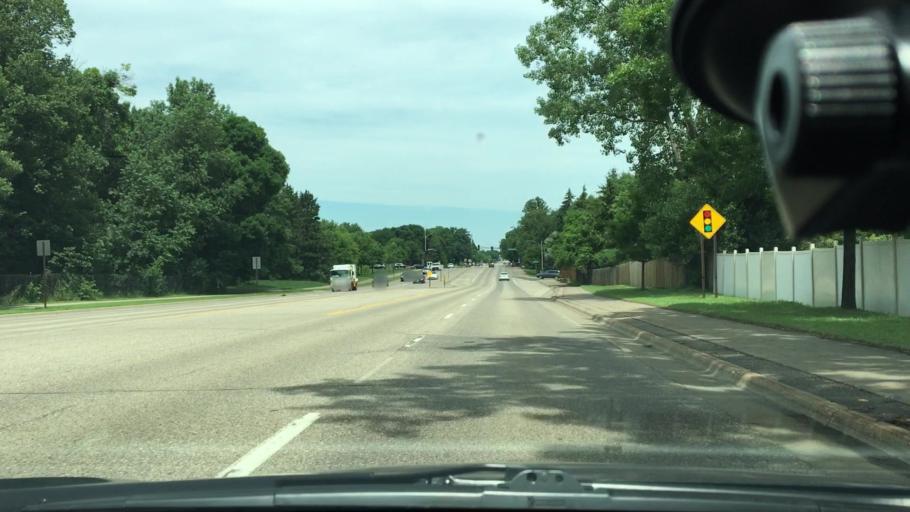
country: US
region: Minnesota
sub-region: Hennepin County
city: Maple Grove
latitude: 45.0706
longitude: -93.4310
